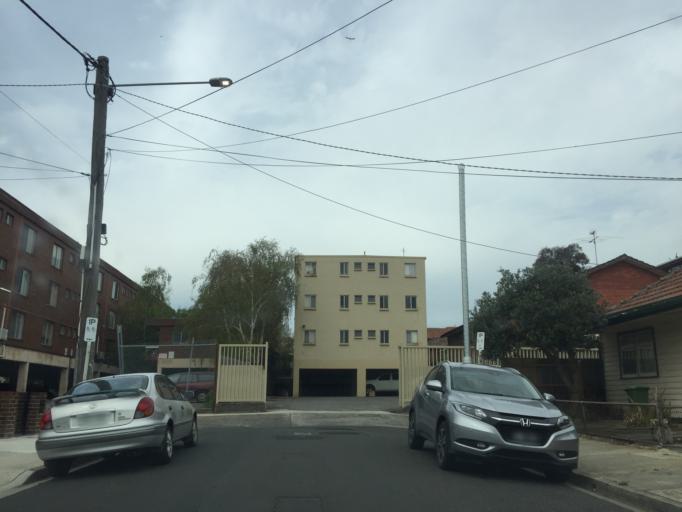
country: AU
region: Victoria
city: Thornbury
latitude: -37.7411
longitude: 145.0052
